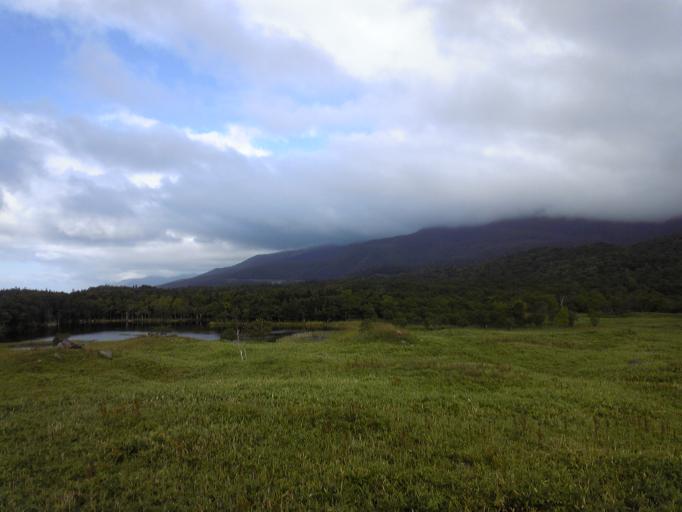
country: JP
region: Hokkaido
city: Shibetsu
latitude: 44.1228
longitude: 145.0758
